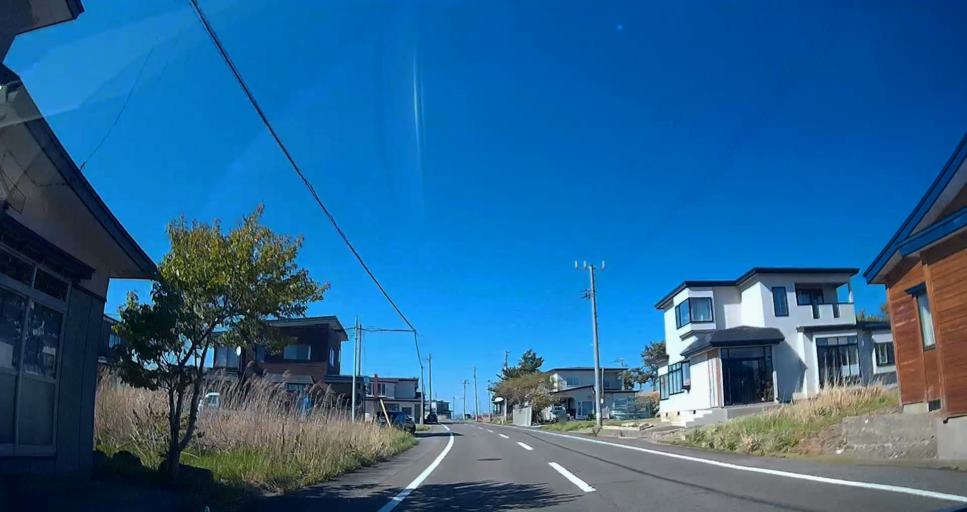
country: JP
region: Hokkaido
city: Hakodate
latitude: 41.5417
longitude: 140.9125
